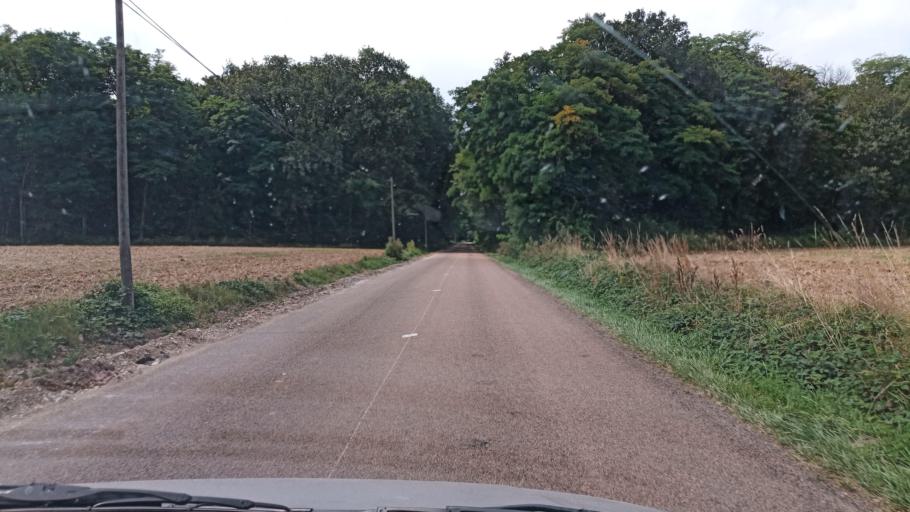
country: FR
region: Bourgogne
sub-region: Departement de l'Yonne
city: Saint-Julien-du-Sault
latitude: 48.0534
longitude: 3.2275
